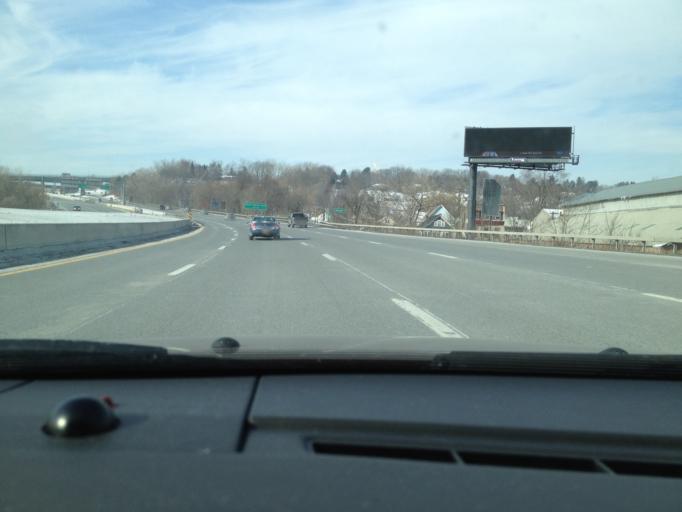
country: US
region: New York
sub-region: Albany County
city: Albany
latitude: 42.6699
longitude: -73.7377
